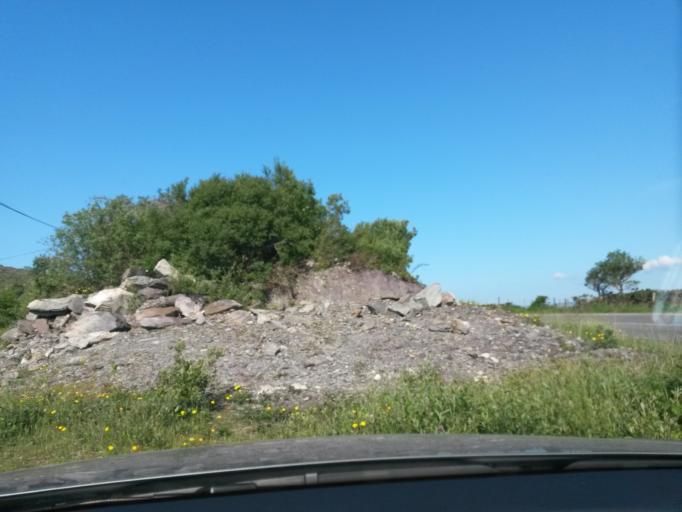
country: IE
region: Munster
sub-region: Ciarrai
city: Kenmare
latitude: 51.7659
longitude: -9.8241
